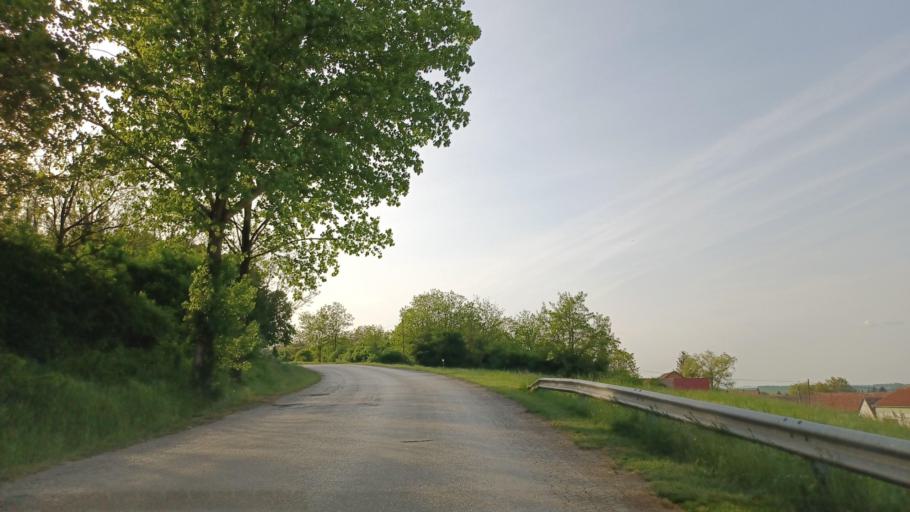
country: HU
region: Baranya
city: Villany
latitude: 45.9549
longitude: 18.3868
